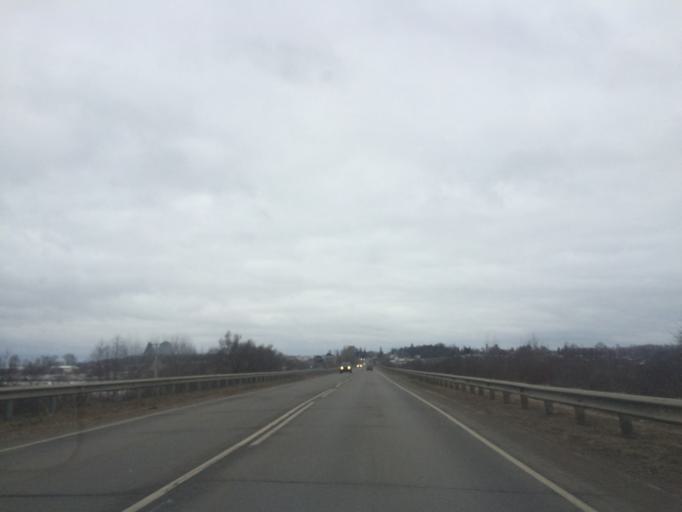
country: RU
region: Tula
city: Krapivna
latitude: 54.1103
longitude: 37.1293
